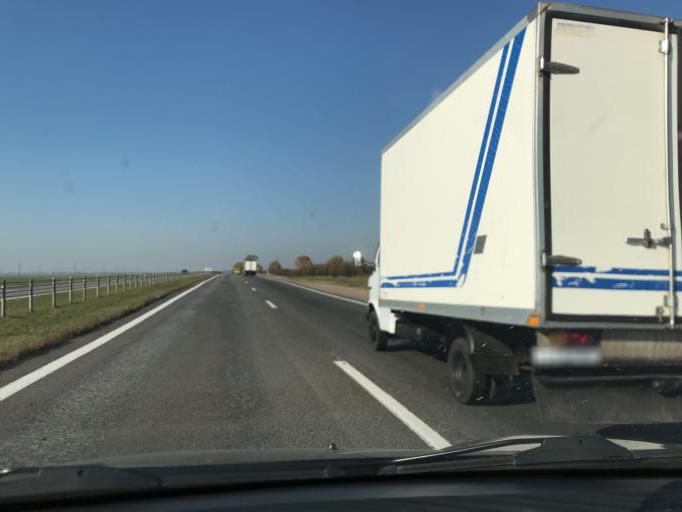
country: BY
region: Minsk
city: Dukora
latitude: 53.6809
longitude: 27.9215
